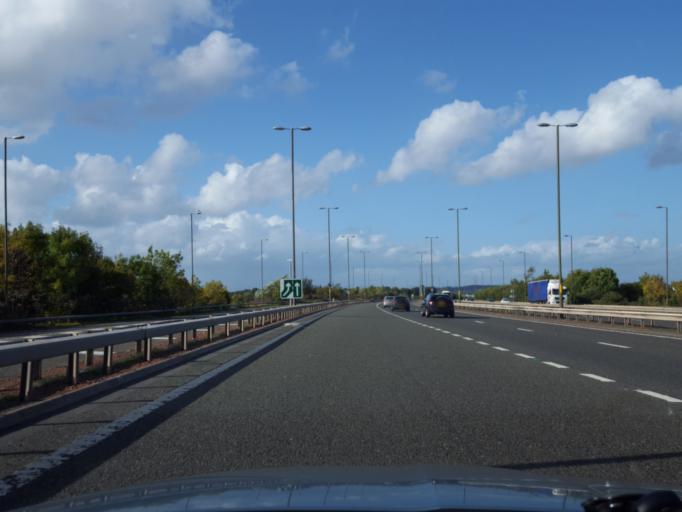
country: GB
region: Scotland
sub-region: Edinburgh
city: Currie
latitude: 55.9274
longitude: -3.3158
